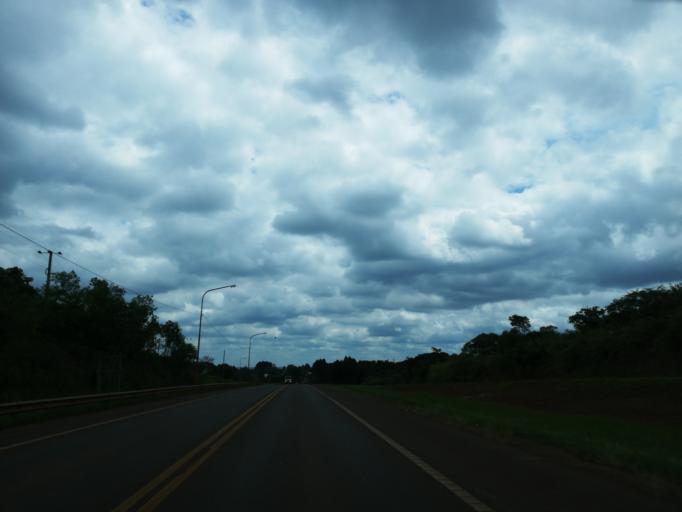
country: AR
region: Misiones
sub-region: Departamento de Leandro N. Alem
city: Leandro N. Alem
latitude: -27.6165
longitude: -55.3240
